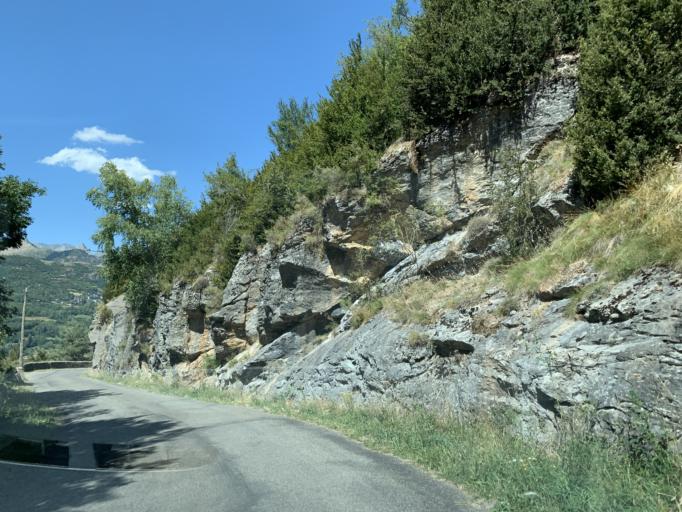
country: ES
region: Aragon
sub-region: Provincia de Huesca
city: Hoz de Jaca
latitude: 42.6932
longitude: -0.3101
